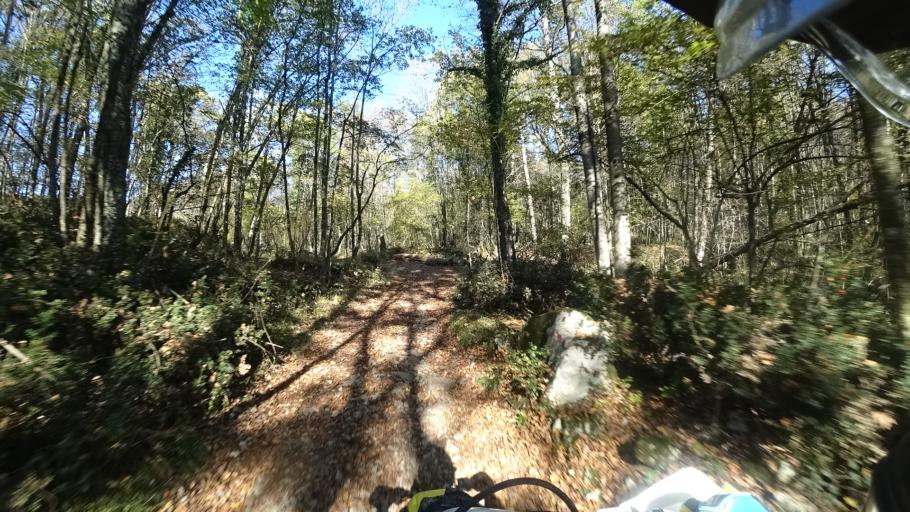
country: HR
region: Primorsko-Goranska
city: Kastav
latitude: 45.3969
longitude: 14.3259
